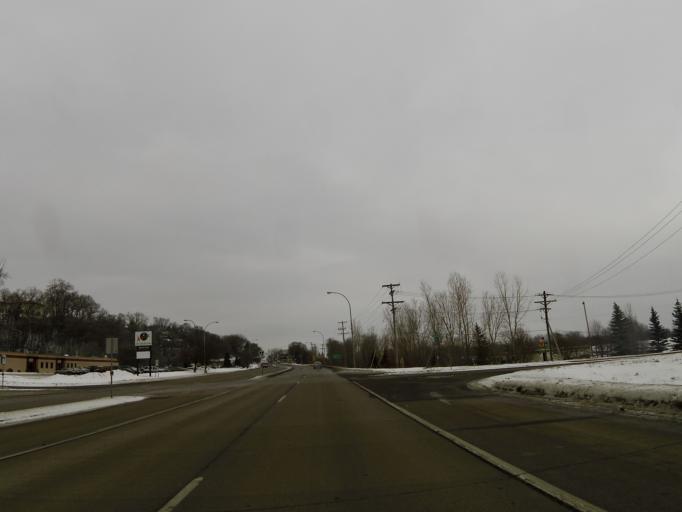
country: US
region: Minnesota
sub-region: Dakota County
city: South Saint Paul
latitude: 44.8963
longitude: -93.0365
